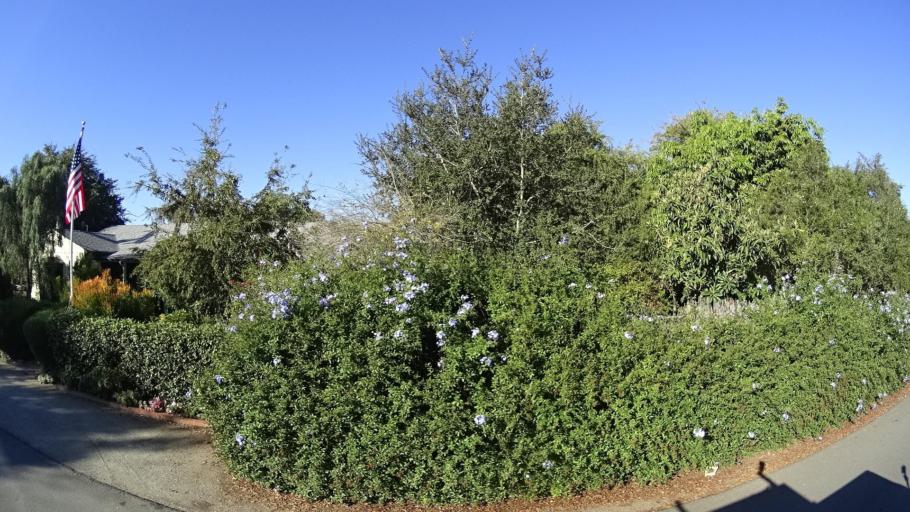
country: US
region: California
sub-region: San Diego County
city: Bonita
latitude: 32.6798
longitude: -117.0226
